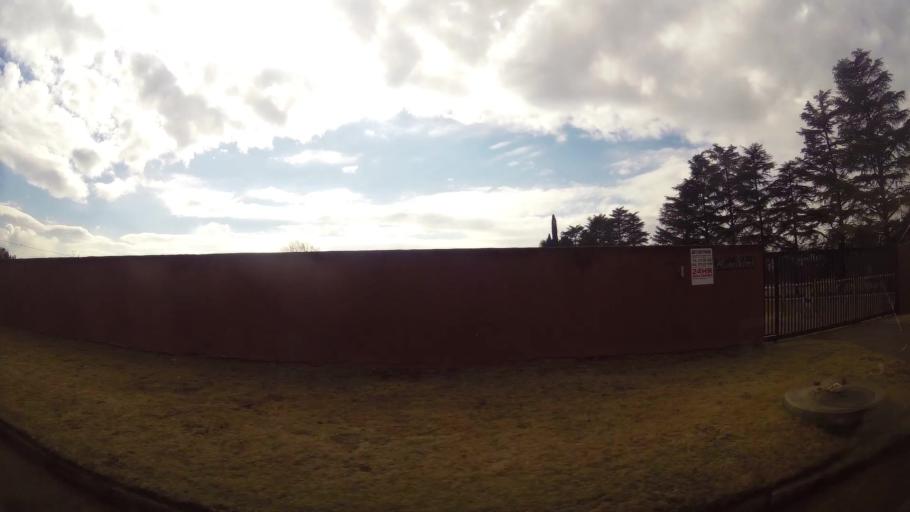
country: ZA
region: Gauteng
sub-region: Sedibeng District Municipality
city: Meyerton
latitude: -26.5873
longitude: 28.0142
